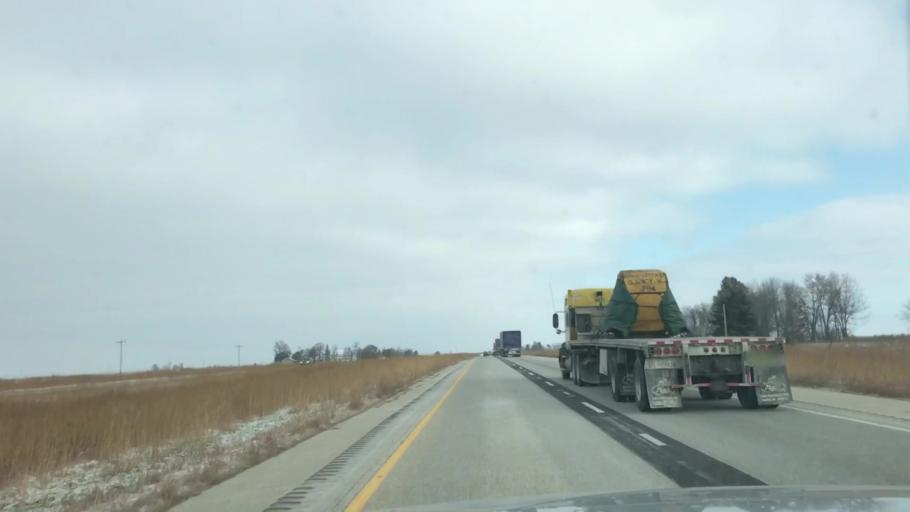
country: US
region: Illinois
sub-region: Sangamon County
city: Divernon
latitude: 39.5085
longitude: -89.6451
